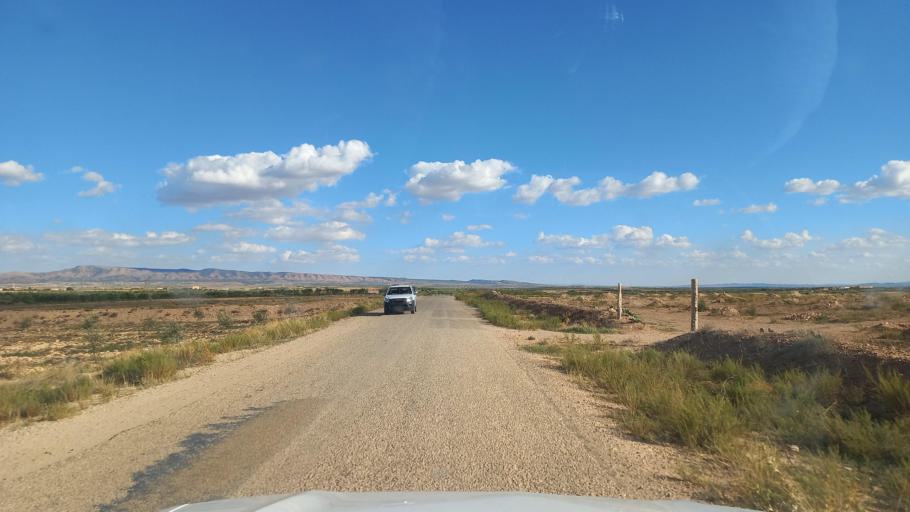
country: TN
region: Al Qasrayn
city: Sbiba
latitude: 35.3906
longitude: 9.0259
